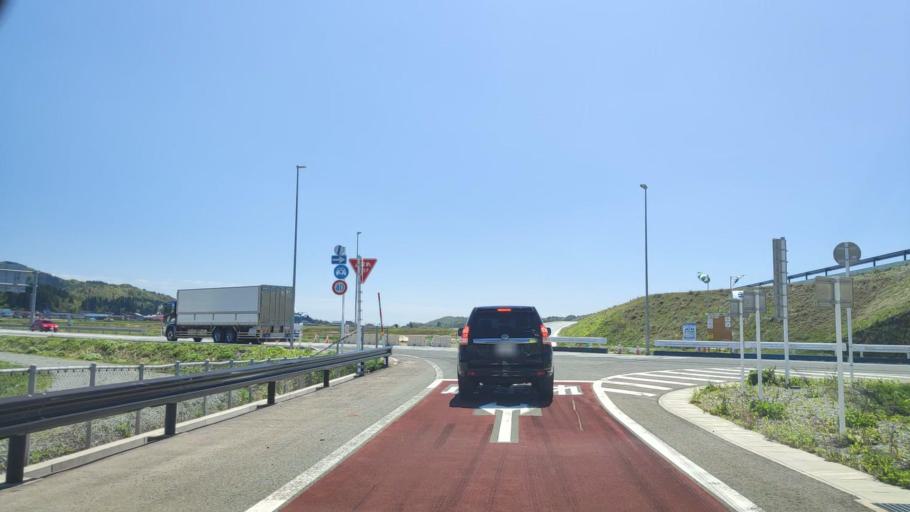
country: JP
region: Yamagata
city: Obanazawa
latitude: 38.5615
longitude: 140.3989
